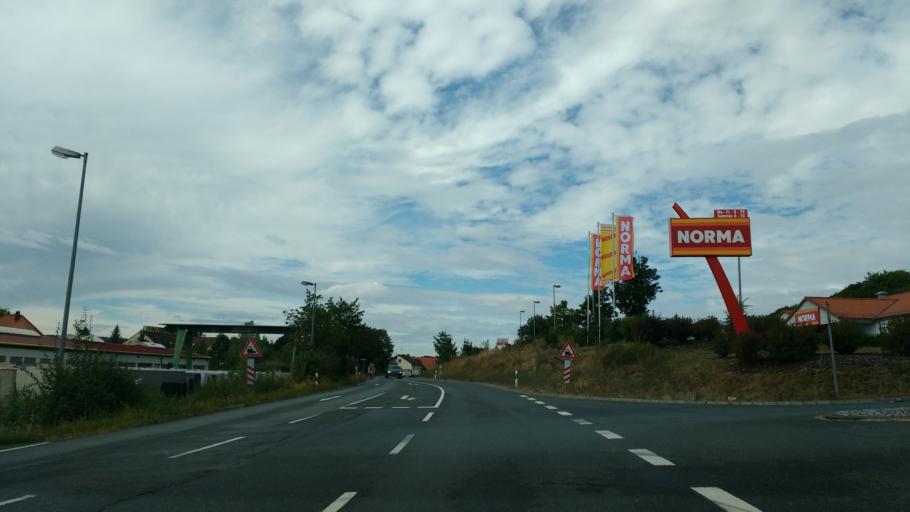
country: DE
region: Bavaria
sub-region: Upper Franconia
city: Schlusselfeld
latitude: 49.7482
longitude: 10.6335
